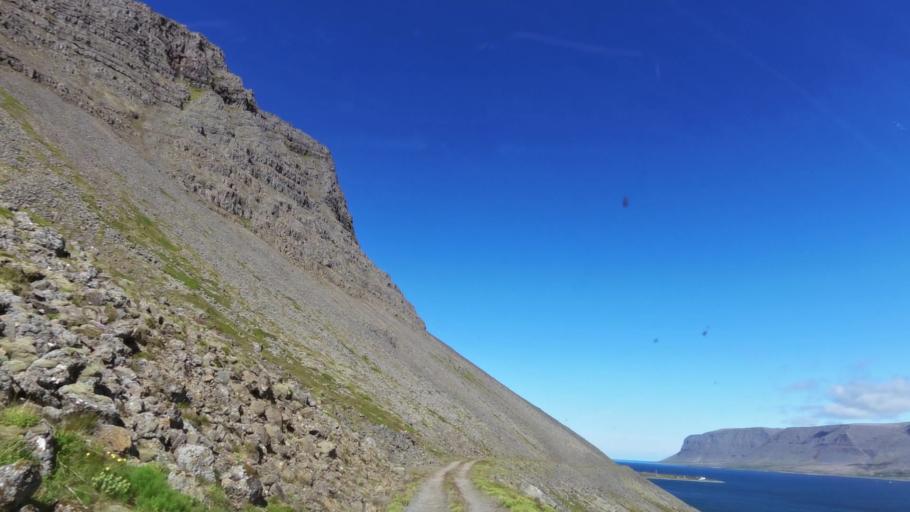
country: IS
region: West
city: Olafsvik
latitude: 65.6297
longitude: -23.9108
